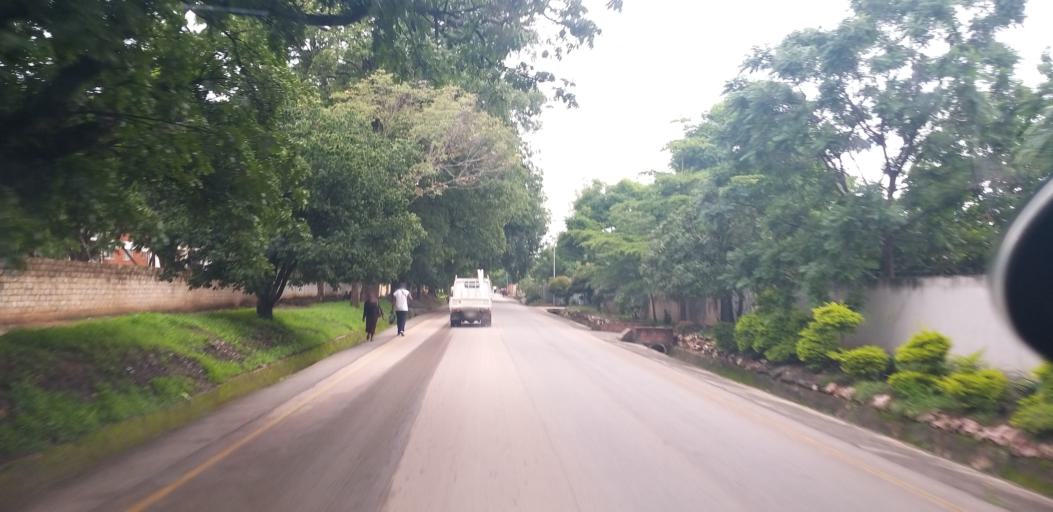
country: ZM
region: Lusaka
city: Lusaka
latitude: -15.4207
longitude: 28.2958
